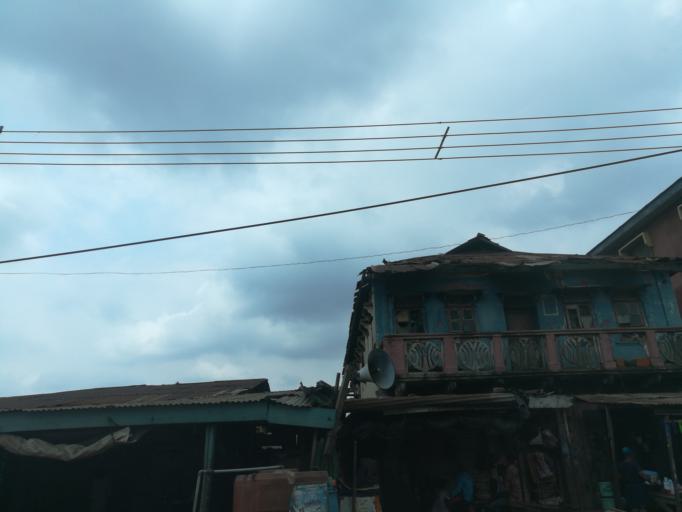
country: NG
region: Lagos
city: Agege
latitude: 6.6187
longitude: 3.3261
